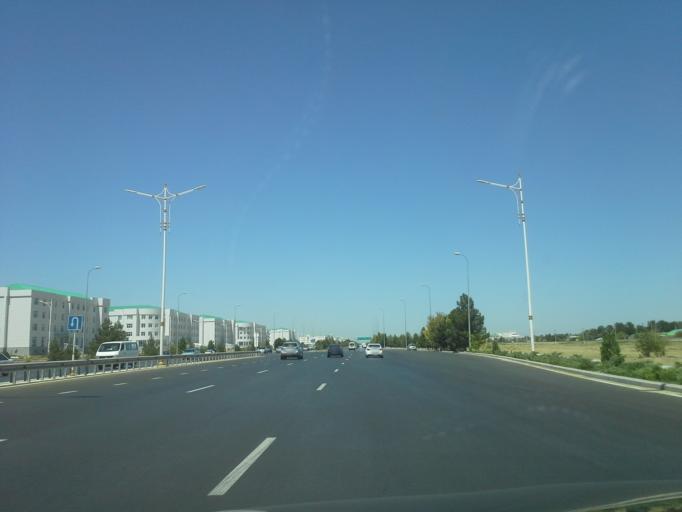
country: TM
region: Ahal
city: Ashgabat
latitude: 37.9811
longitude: 58.3368
